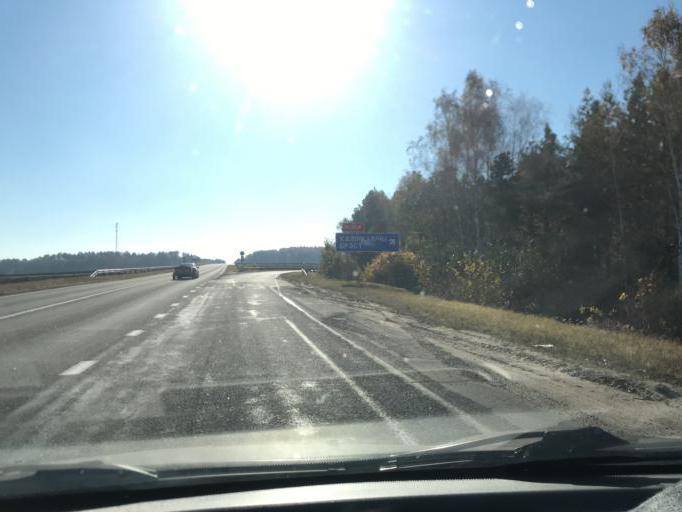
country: BY
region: Gomel
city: Gomel
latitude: 52.3919
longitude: 30.8282
